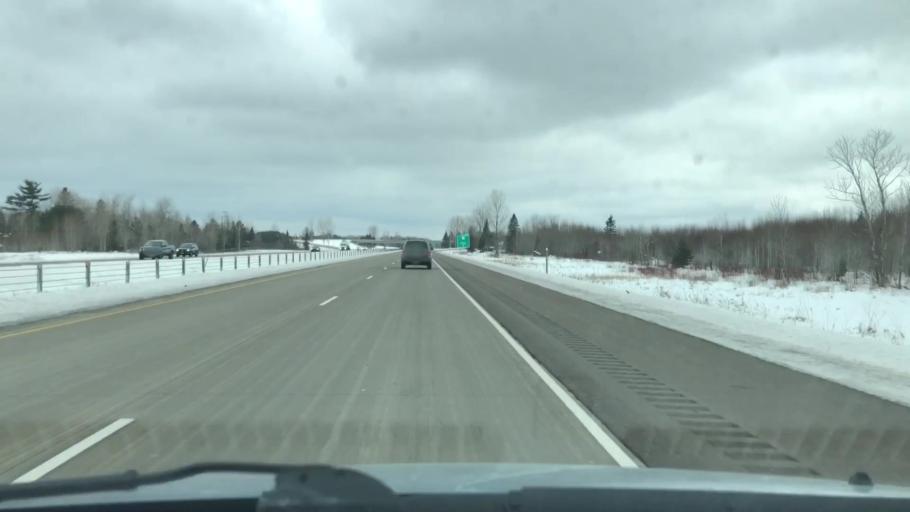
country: US
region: Minnesota
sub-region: Carlton County
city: Esko
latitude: 46.6974
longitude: -92.3567
